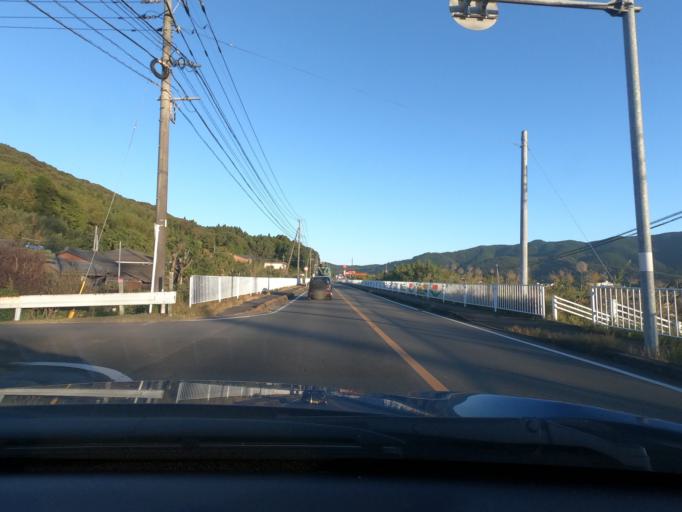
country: JP
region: Kagoshima
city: Satsumasendai
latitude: 31.8075
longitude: 130.3405
